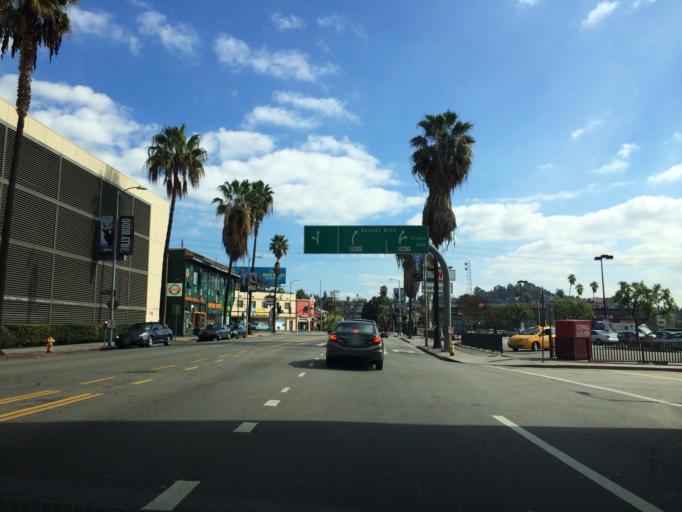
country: US
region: California
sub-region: Los Angeles County
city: Silver Lake
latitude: 34.0981
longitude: -118.2889
